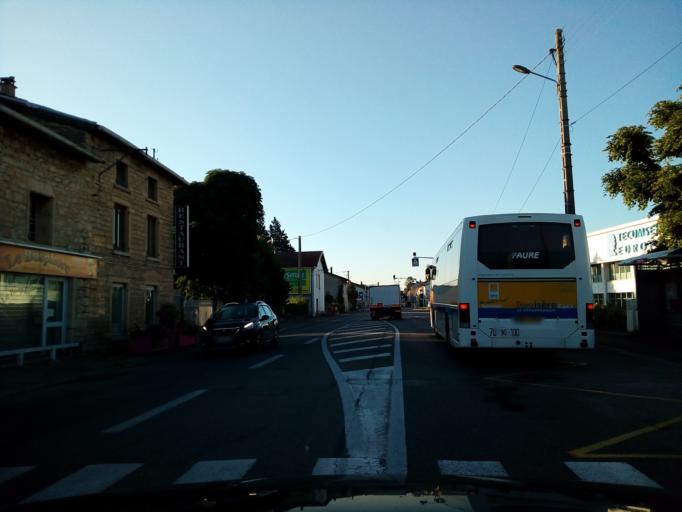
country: FR
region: Rhone-Alpes
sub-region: Departement de l'Isere
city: La Verpilliere
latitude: 45.6401
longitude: 5.1387
